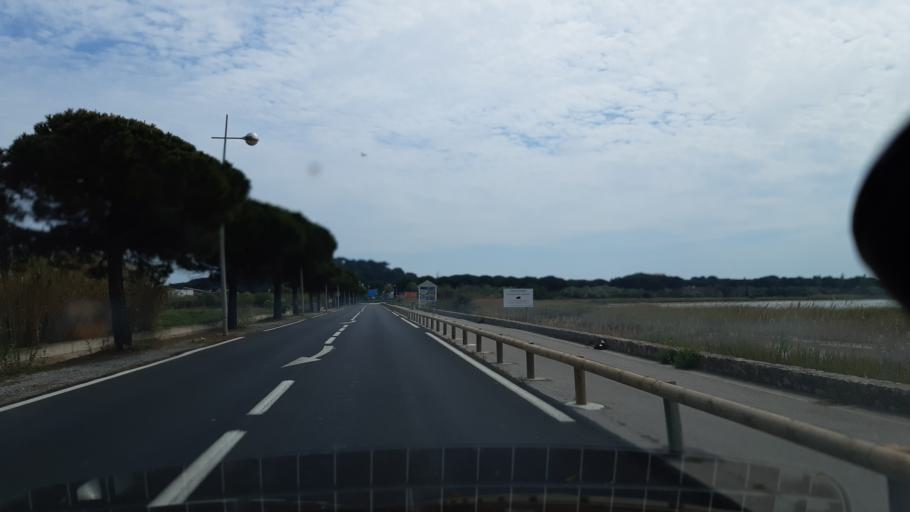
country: FR
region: Languedoc-Roussillon
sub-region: Departement de l'Aude
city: Gruissan
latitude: 43.1162
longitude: 3.0896
